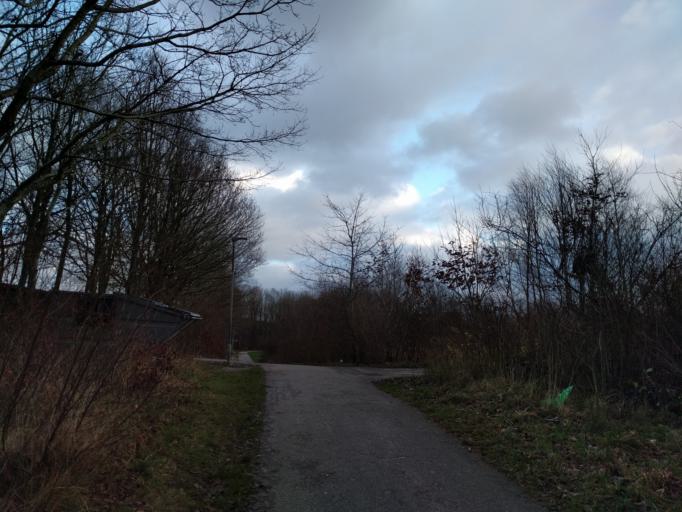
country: DK
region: Central Jutland
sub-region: Silkeborg Kommune
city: Silkeborg
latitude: 56.1898
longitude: 9.5238
